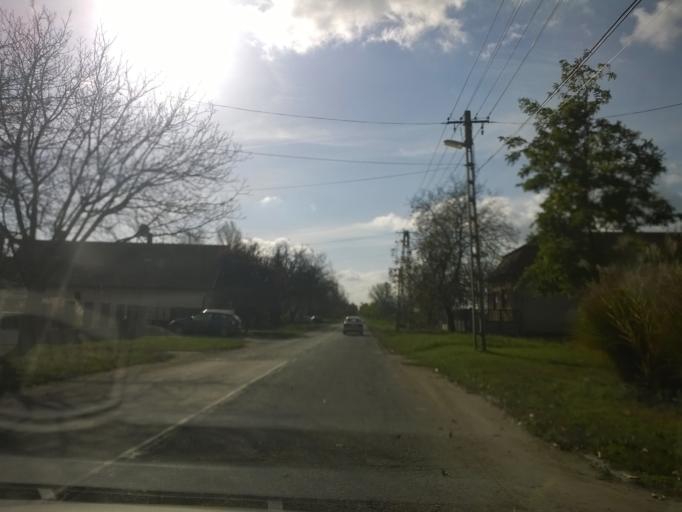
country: HU
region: Pest
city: Kiskunlachaza
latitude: 47.1659
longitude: 18.9977
